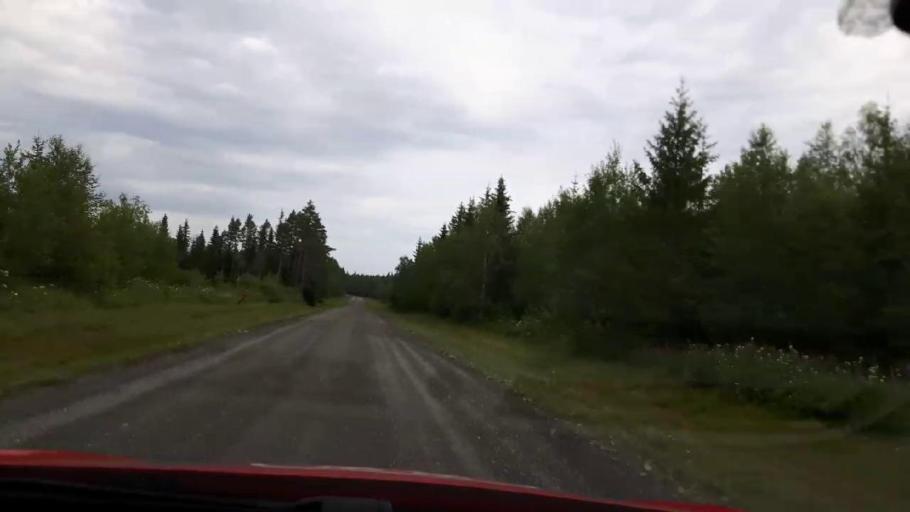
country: SE
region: Jaemtland
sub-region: Stroemsunds Kommun
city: Stroemsund
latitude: 63.7499
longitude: 15.5916
